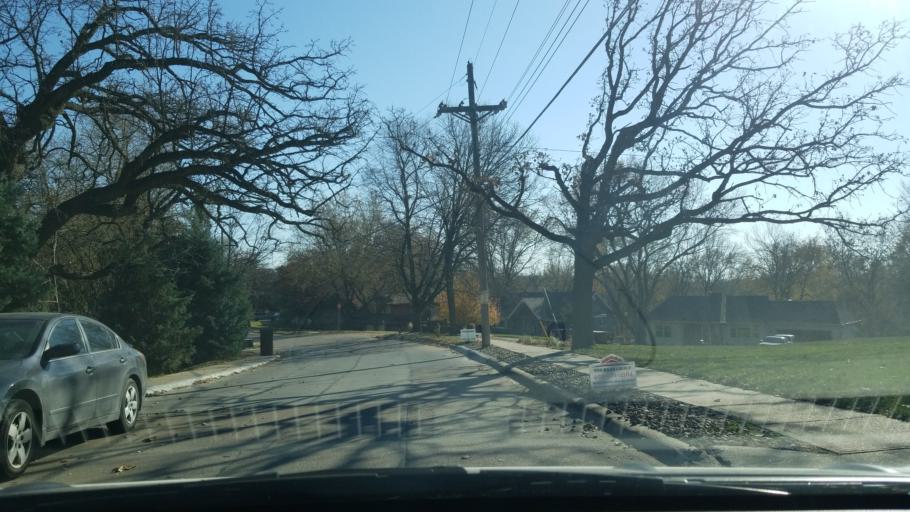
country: US
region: Nebraska
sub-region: Sarpy County
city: Bellevue
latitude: 41.1589
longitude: -95.9023
